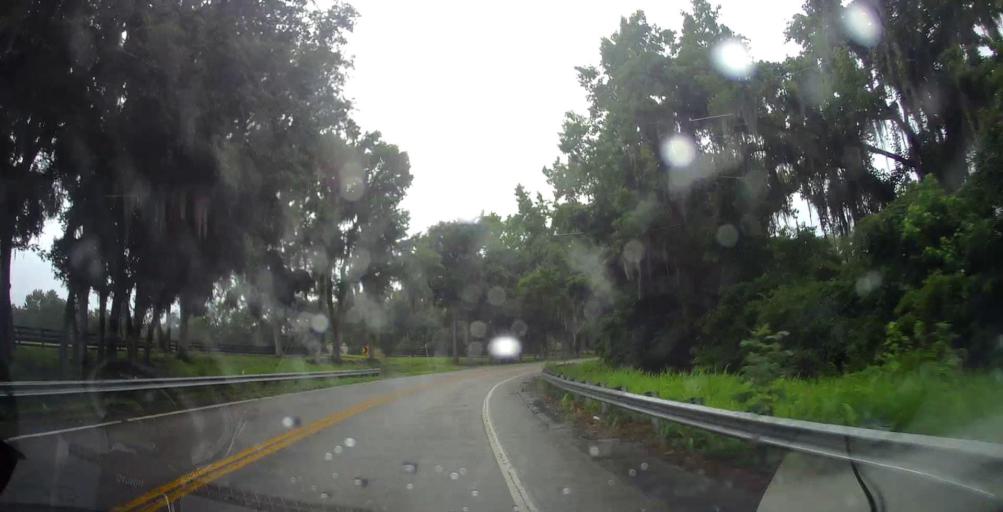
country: US
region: Florida
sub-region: Marion County
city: Citra
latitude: 29.3728
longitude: -82.2503
